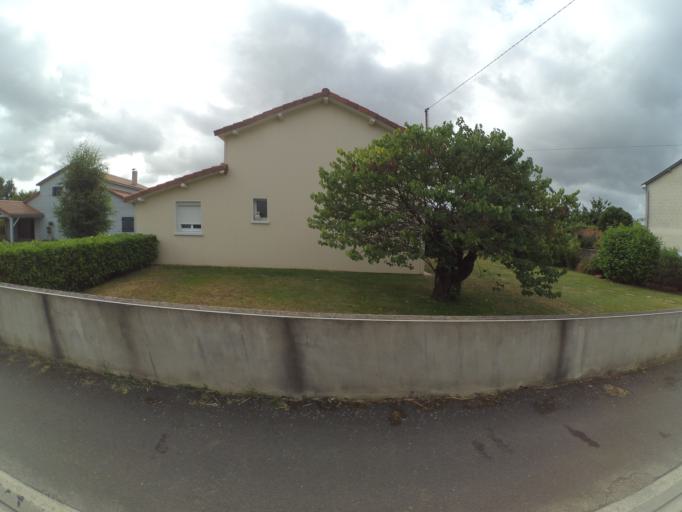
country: FR
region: Pays de la Loire
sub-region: Departement de Maine-et-Loire
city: Villedieu-la-Blouere
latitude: 47.1451
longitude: -1.0660
